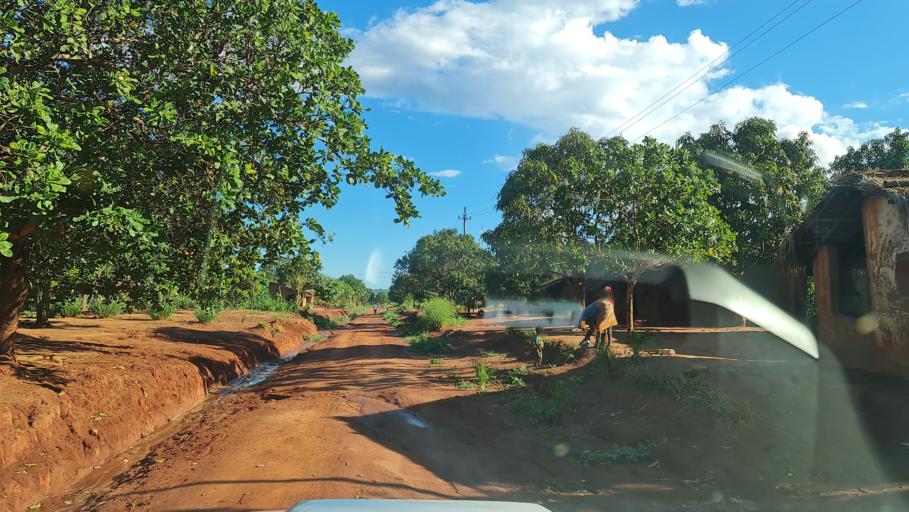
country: MZ
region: Nampula
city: Ilha de Mocambique
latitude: -14.9199
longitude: 40.2178
